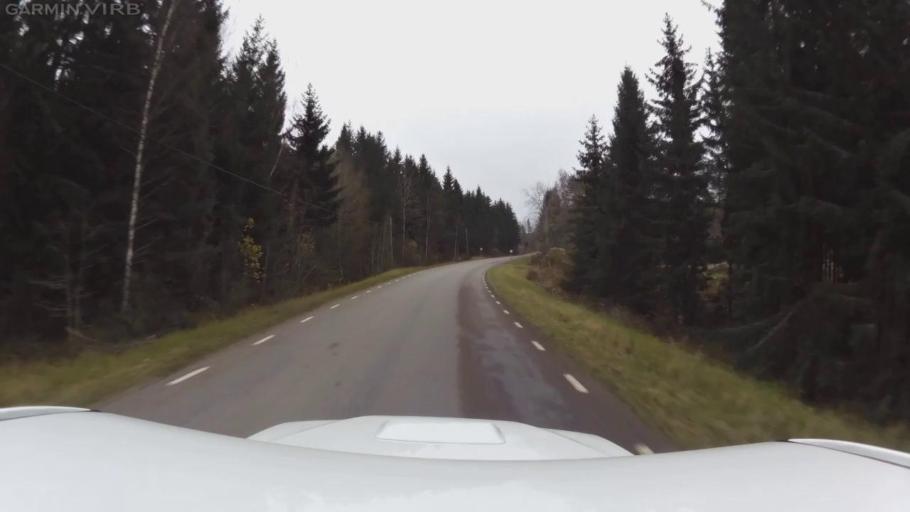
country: SE
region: OEstergoetland
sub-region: Linkopings Kommun
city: Vikingstad
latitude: 58.2507
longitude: 15.3860
